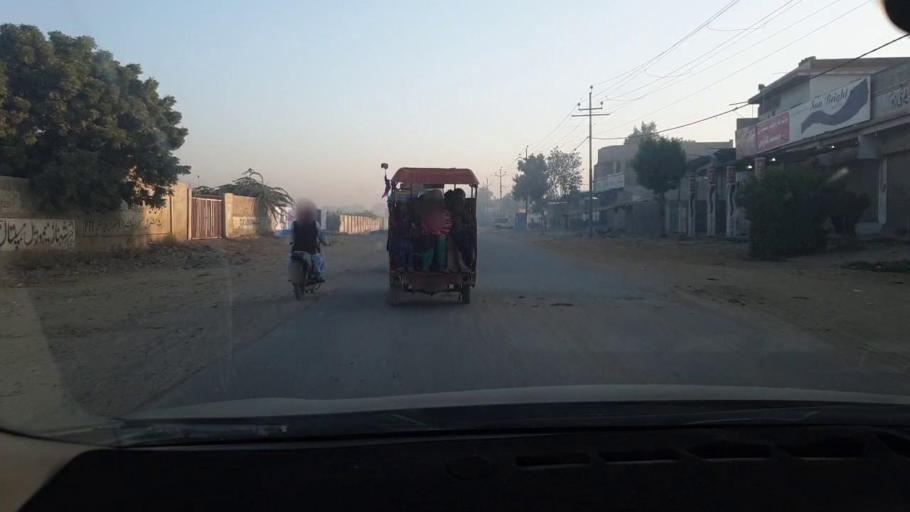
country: PK
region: Sindh
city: Malir Cantonment
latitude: 25.0023
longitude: 67.1503
